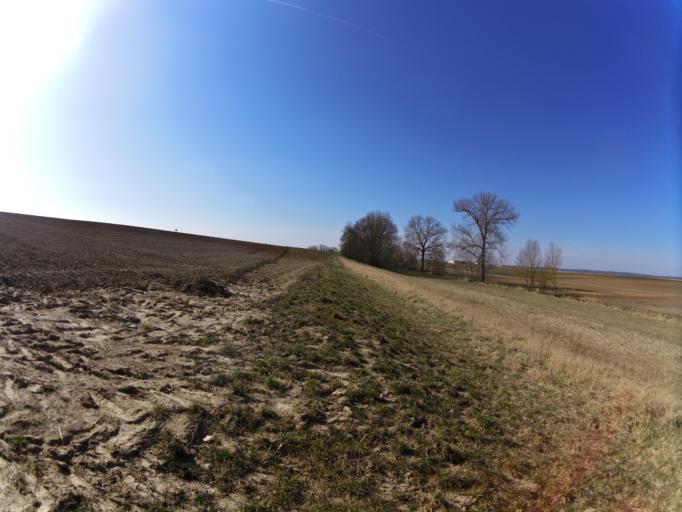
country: DE
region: Bavaria
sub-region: Regierungsbezirk Unterfranken
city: Oberpleichfeld
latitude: 49.8755
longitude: 10.0724
